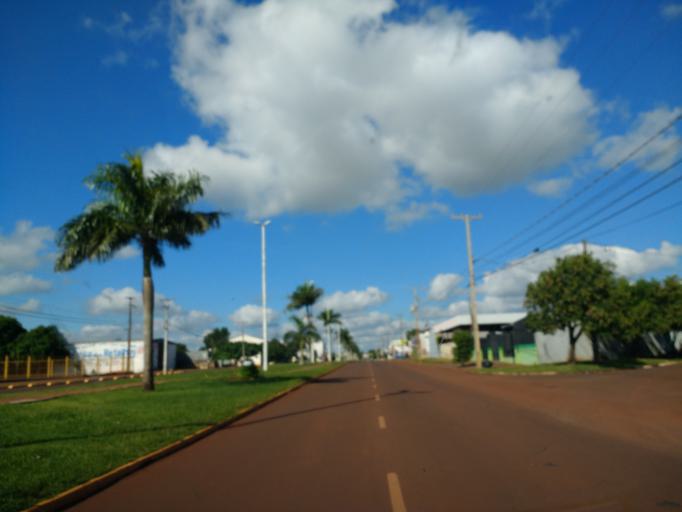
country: BR
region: Parana
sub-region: Palotina
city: Palotina
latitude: -24.4090
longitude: -53.5327
